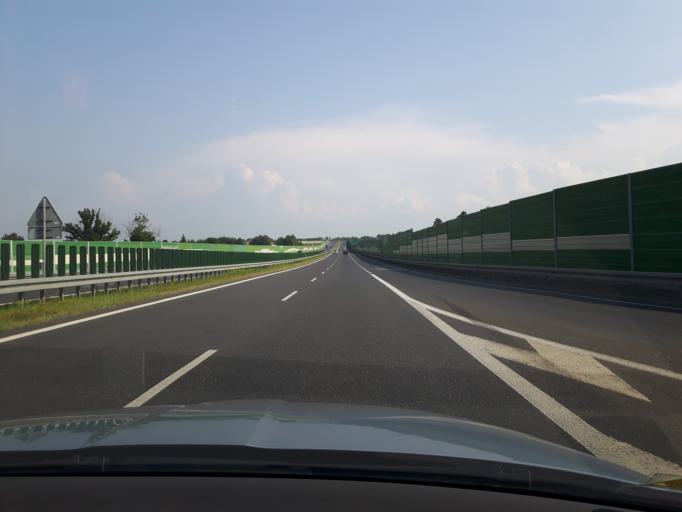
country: PL
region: Masovian Voivodeship
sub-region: Powiat plonski
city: Plonsk
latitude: 52.6114
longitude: 20.3912
